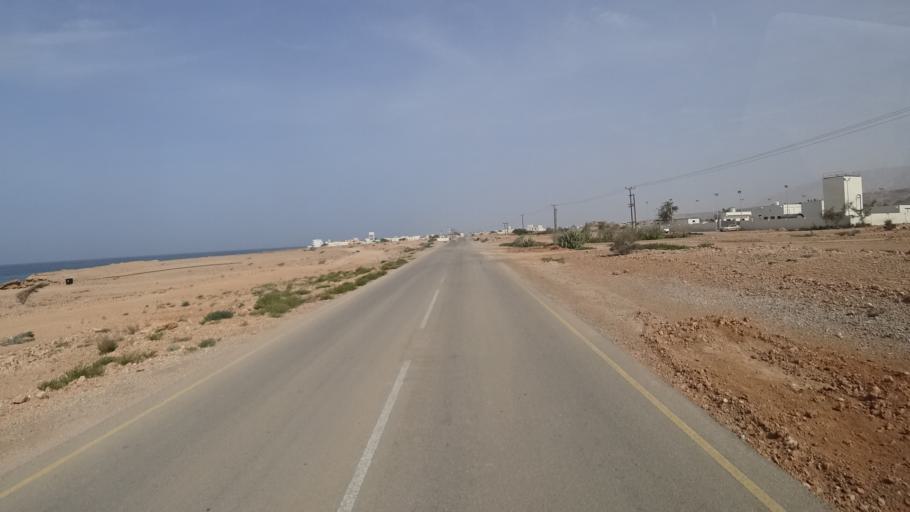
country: OM
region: Ash Sharqiyah
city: Sur
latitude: 22.9957
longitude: 59.1289
